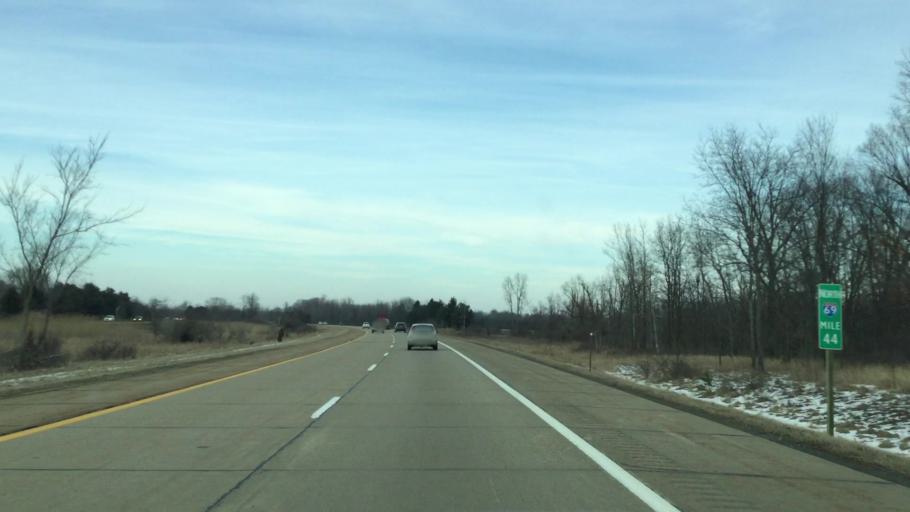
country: US
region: Michigan
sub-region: Eaton County
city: Olivet
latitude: 42.3774
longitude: -84.9708
